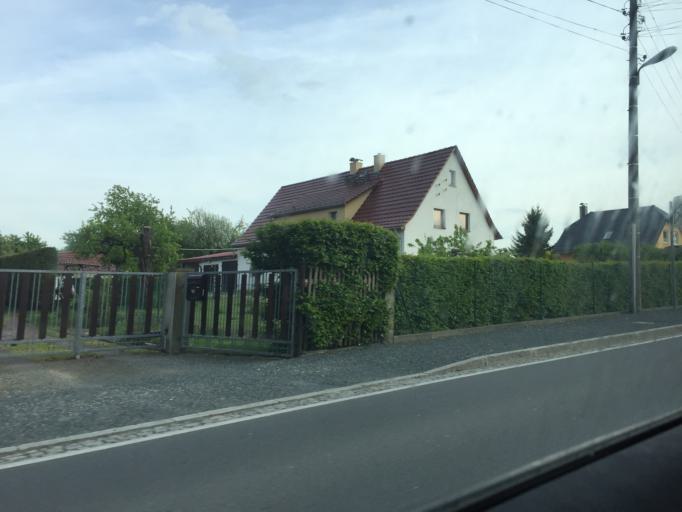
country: DE
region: Saxony
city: Lohmen
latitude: 50.9867
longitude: 13.9883
